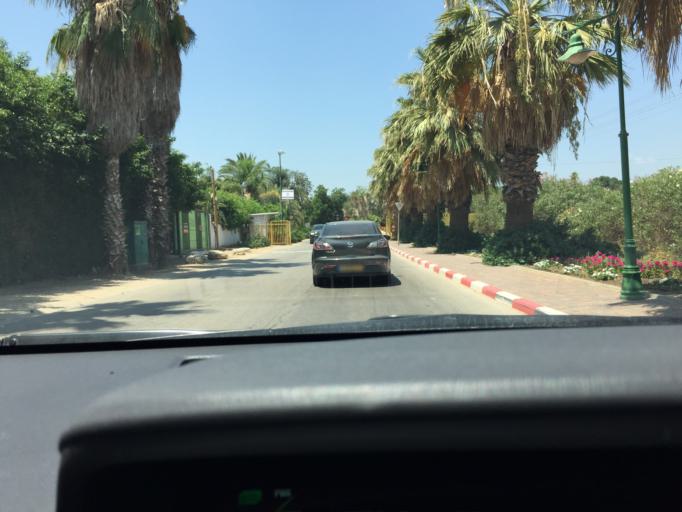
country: IL
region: Central District
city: Nehalim
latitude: 32.0509
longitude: 34.9036
